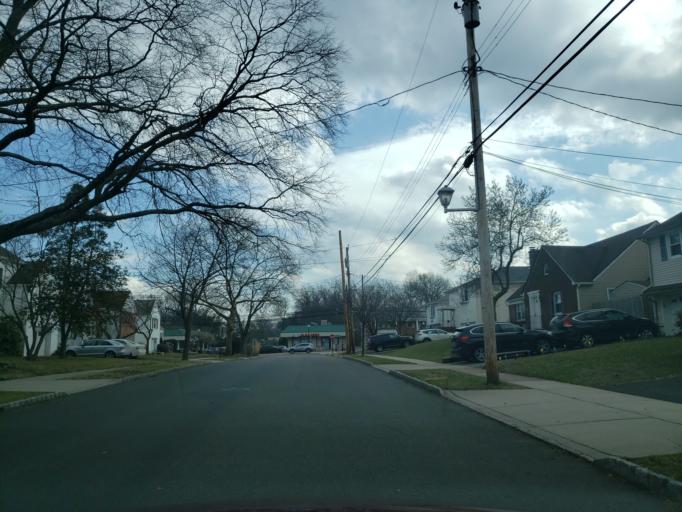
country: US
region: New Jersey
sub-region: Union County
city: Springfield
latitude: 40.6910
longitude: -74.3325
